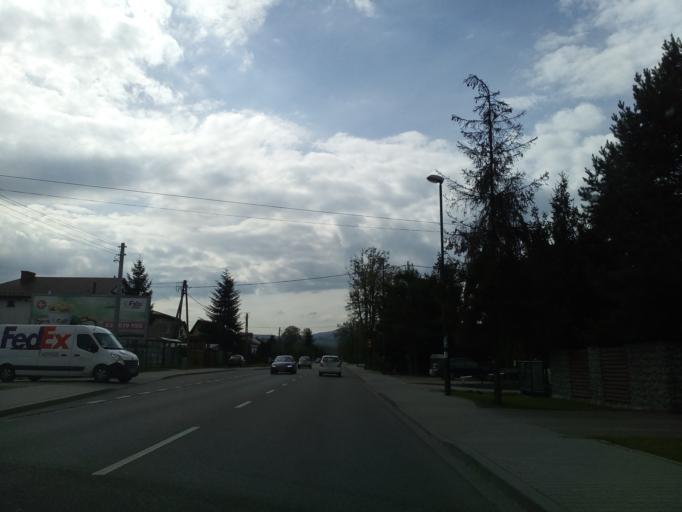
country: PL
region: Lesser Poland Voivodeship
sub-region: Powiat nowosadecki
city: Nawojowa
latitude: 49.5741
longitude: 20.7335
